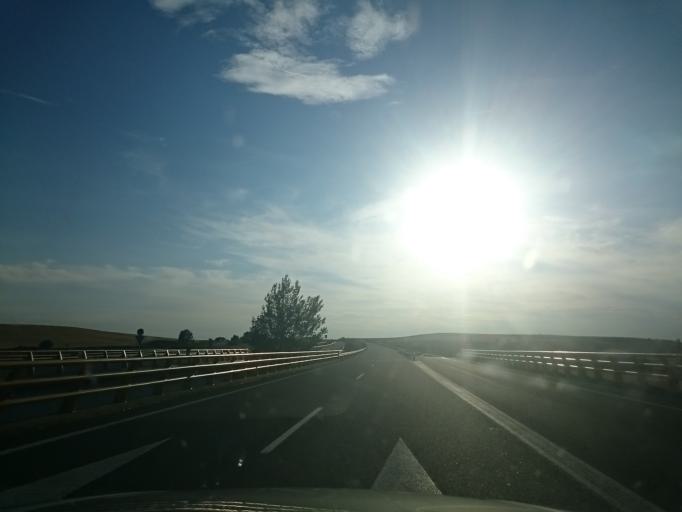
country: ES
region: Castille and Leon
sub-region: Provincia de Palencia
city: Ledigos
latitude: 42.3670
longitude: -4.8696
